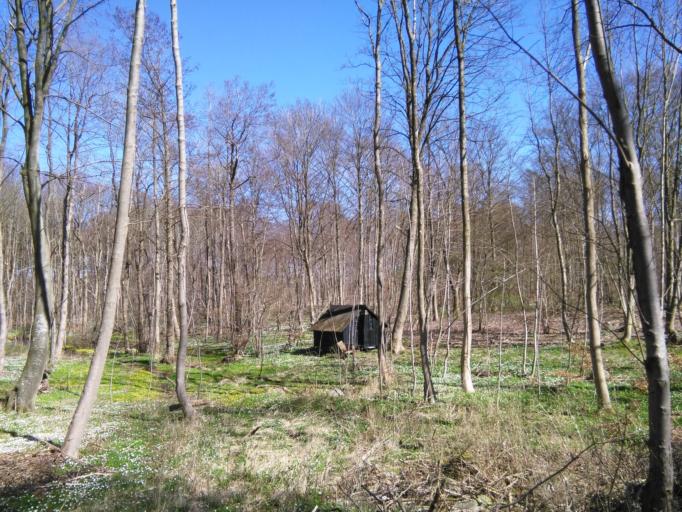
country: DK
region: Central Jutland
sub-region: Arhus Kommune
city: Beder
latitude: 56.0666
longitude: 10.2397
